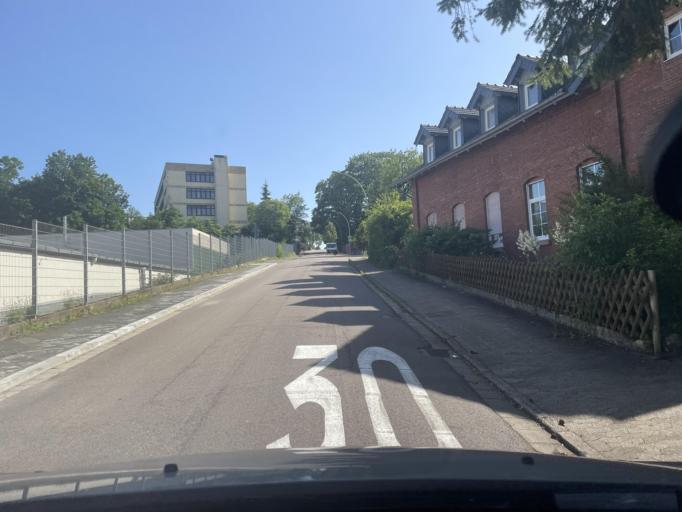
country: DE
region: Saarland
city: Sankt Ingbert
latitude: 49.2725
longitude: 7.1050
